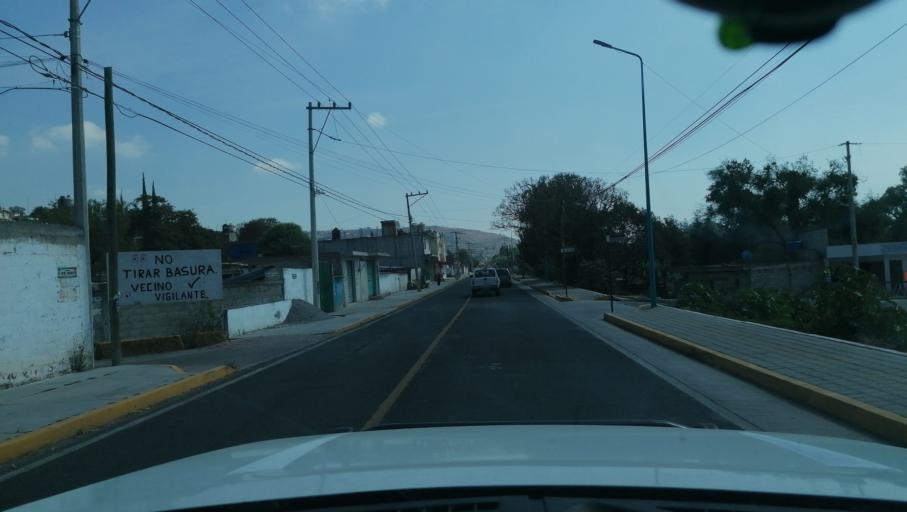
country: MX
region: Tlaxcala
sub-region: San Jeronimo Zacualpan
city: San Jeronimo Zacualpan
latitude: 19.2393
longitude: -98.2697
